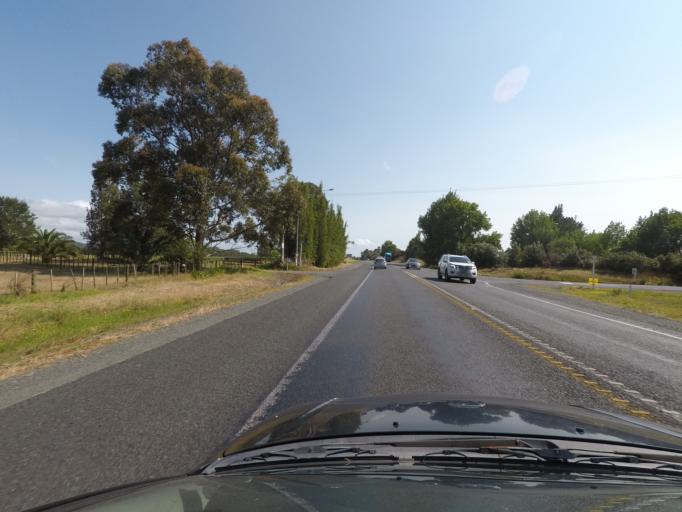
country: NZ
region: Northland
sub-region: Whangarei
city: Ruakaka
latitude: -35.9556
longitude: 174.4516
